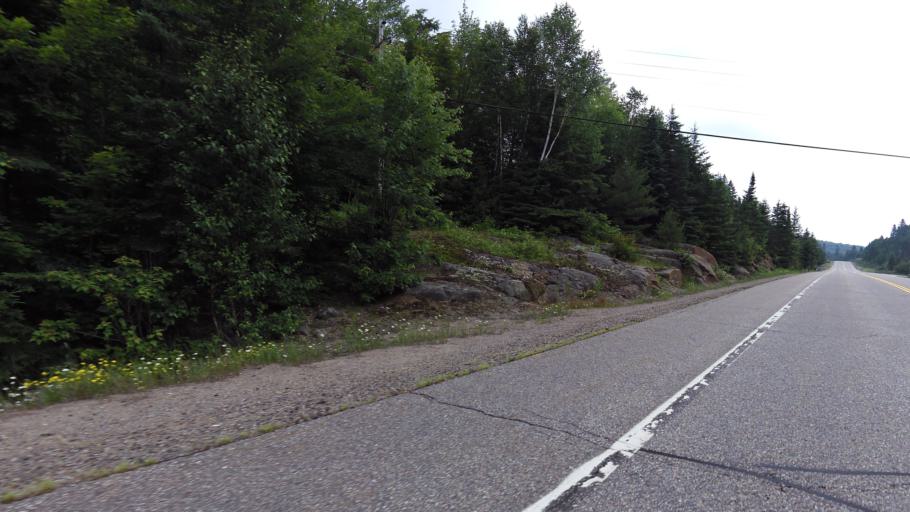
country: CA
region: Ontario
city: Huntsville
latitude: 45.5650
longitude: -78.5538
